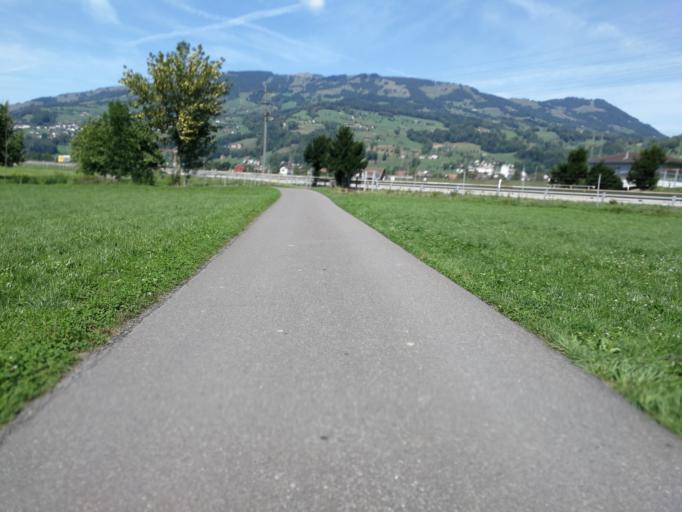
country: CH
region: Schwyz
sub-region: Bezirk Schwyz
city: Steinen
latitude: 47.0380
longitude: 8.6154
